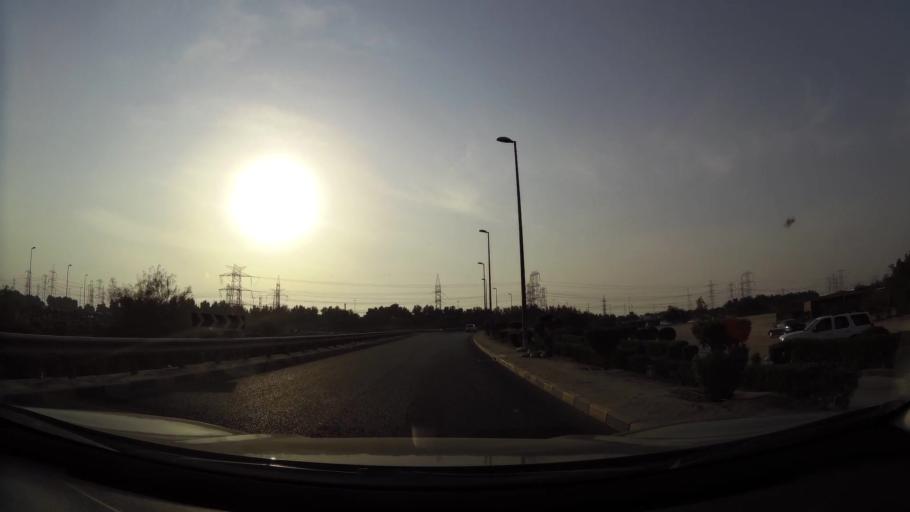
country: KW
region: Mubarak al Kabir
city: Sabah as Salim
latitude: 29.2205
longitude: 48.0581
